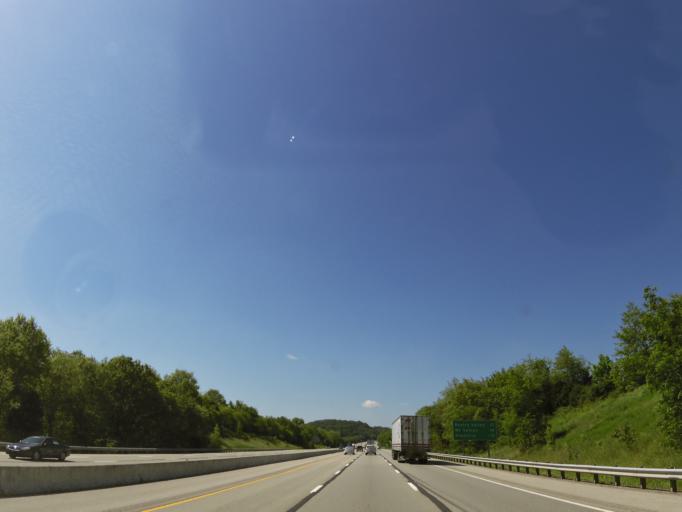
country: US
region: Kentucky
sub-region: Madison County
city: Berea
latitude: 37.5570
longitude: -84.3163
